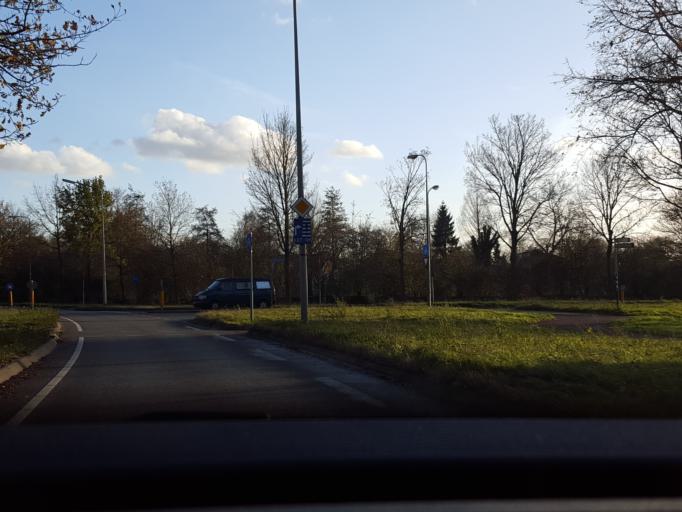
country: NL
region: Gelderland
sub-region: Gemeente Zutphen
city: Zutphen
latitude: 52.1290
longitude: 6.1957
